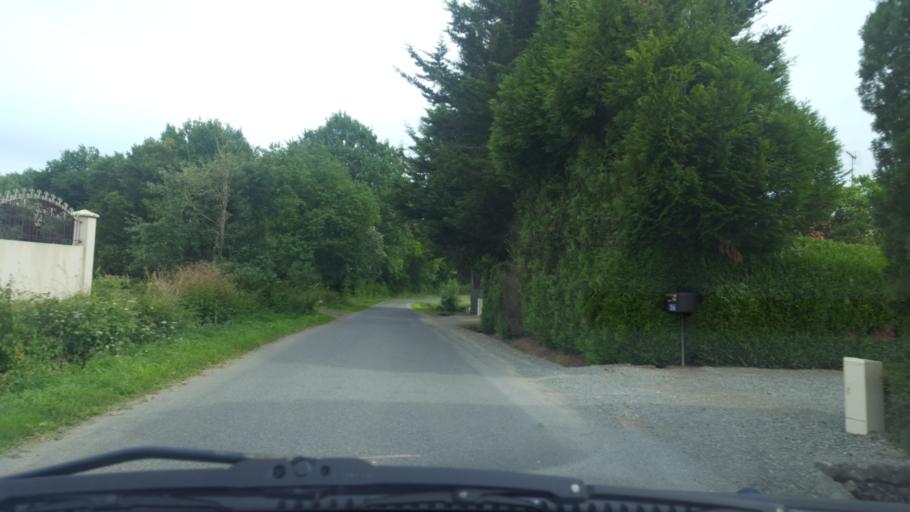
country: FR
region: Pays de la Loire
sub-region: Departement de la Loire-Atlantique
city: La Limouziniere
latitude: 47.0028
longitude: -1.5841
